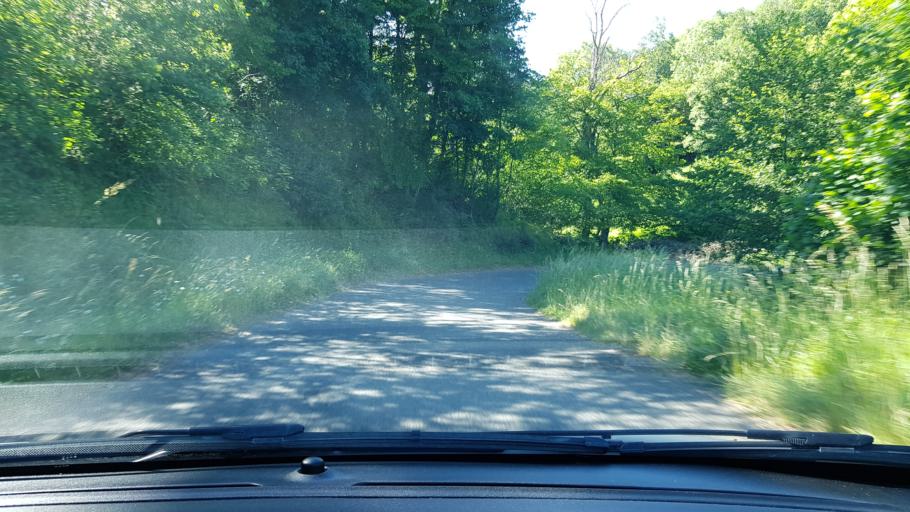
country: FR
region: Rhone-Alpes
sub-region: Departement du Rhone
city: Saint-Didier-sous-Riverie
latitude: 45.5900
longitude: 4.5878
